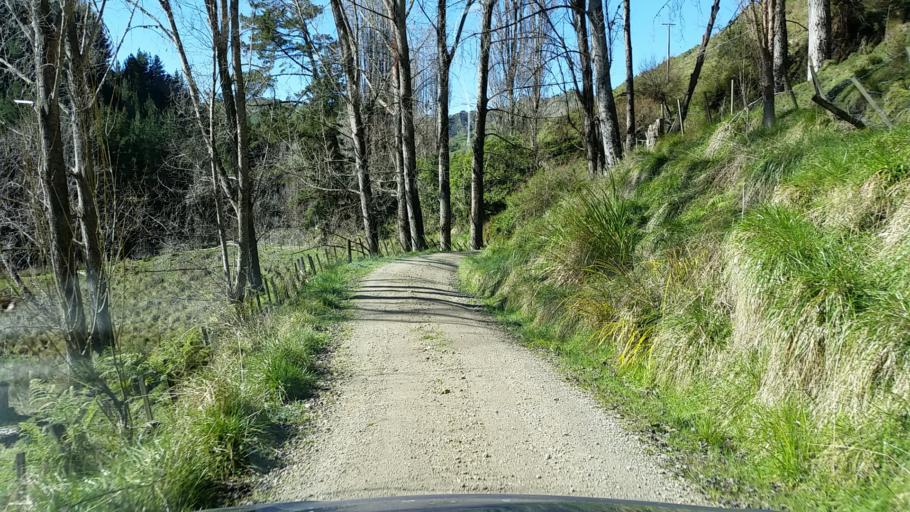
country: NZ
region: Taranaki
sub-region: South Taranaki District
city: Patea
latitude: -39.6209
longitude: 174.8249
